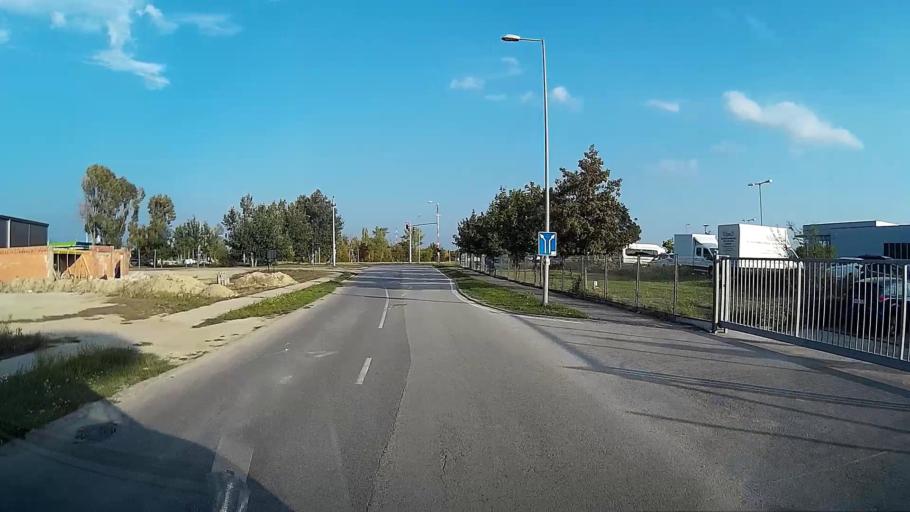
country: HU
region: Pest
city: Budakalasz
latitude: 47.6415
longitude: 19.0658
